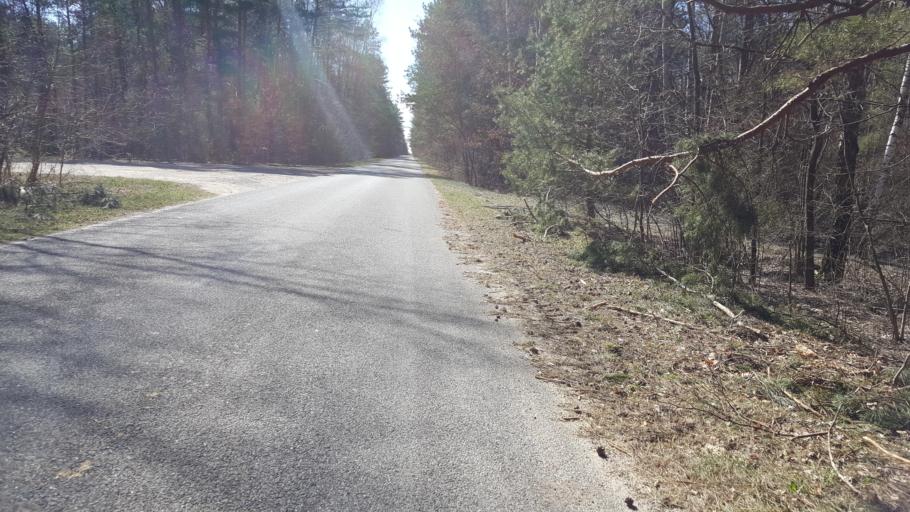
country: BY
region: Brest
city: Kamyanyets
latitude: 52.2982
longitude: 23.8286
